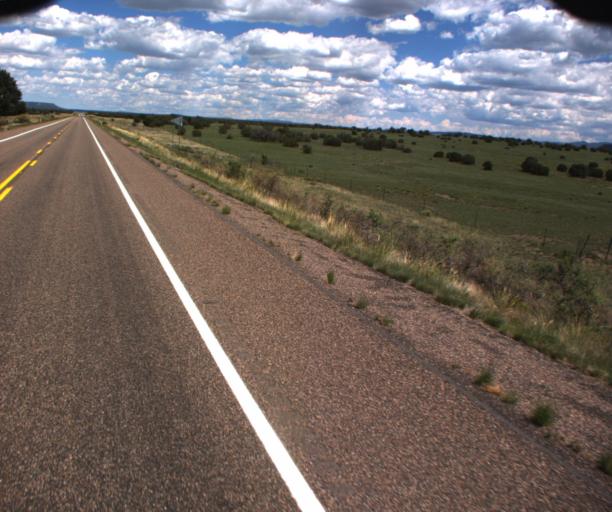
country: US
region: Arizona
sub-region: Apache County
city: Springerville
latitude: 34.1465
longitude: -109.2039
